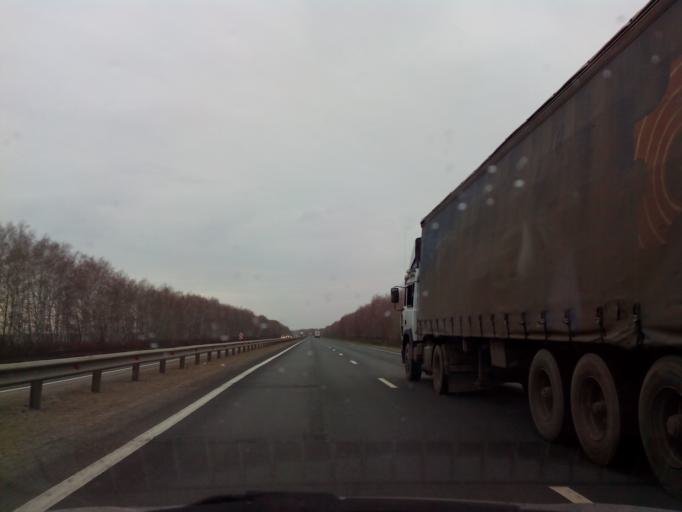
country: RU
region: Tambov
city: Selezni
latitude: 52.7620
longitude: 41.1248
